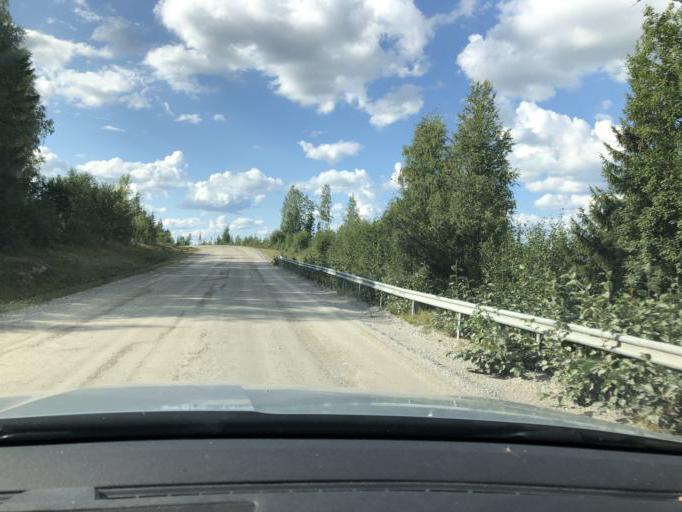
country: SE
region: Vaesternorrland
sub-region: Solleftea Kommun
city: Solleftea
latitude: 63.3179
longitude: 17.2397
